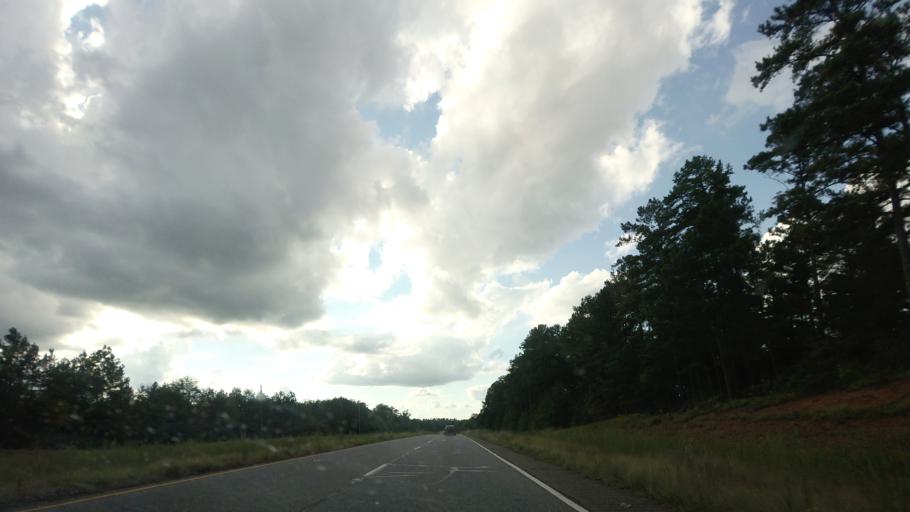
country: US
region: Georgia
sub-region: Houston County
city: Perry
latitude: 32.4154
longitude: -83.6879
